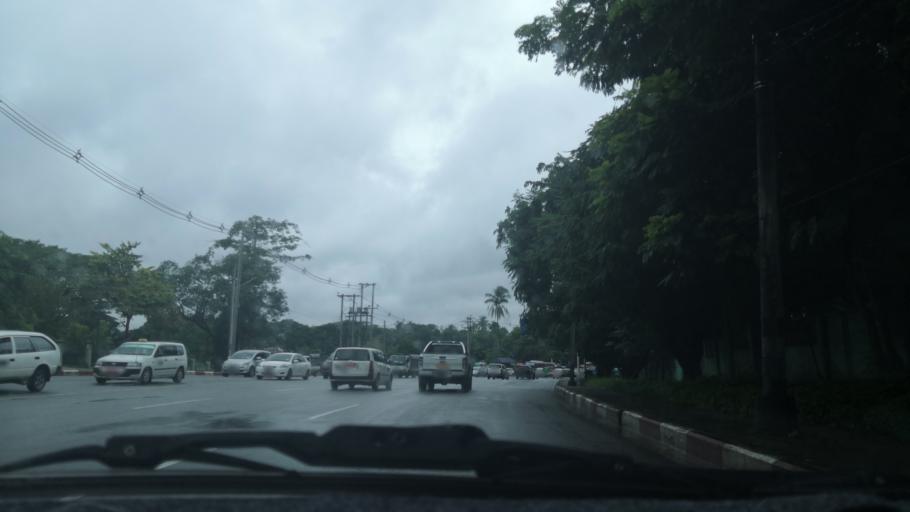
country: MM
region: Yangon
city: Yangon
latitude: 16.8909
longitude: 96.1203
